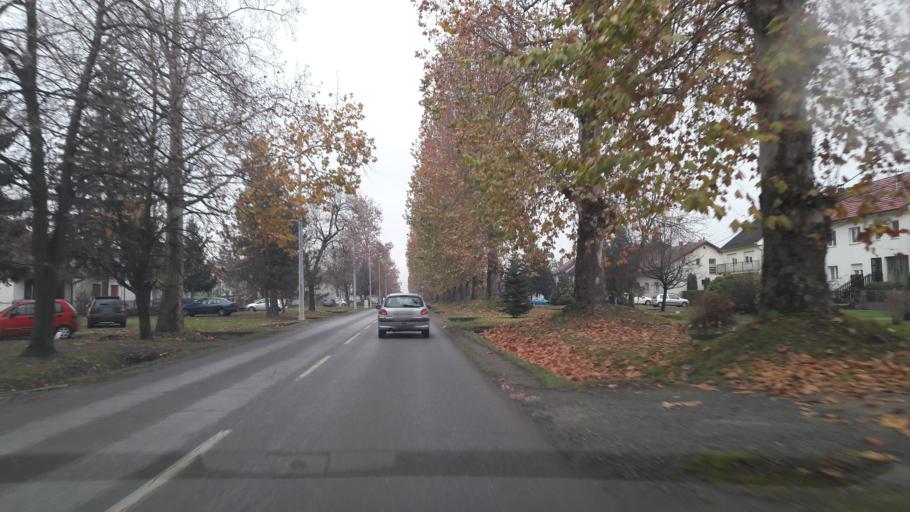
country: HR
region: Osjecko-Baranjska
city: Visnjevac
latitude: 45.5704
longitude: 18.6091
